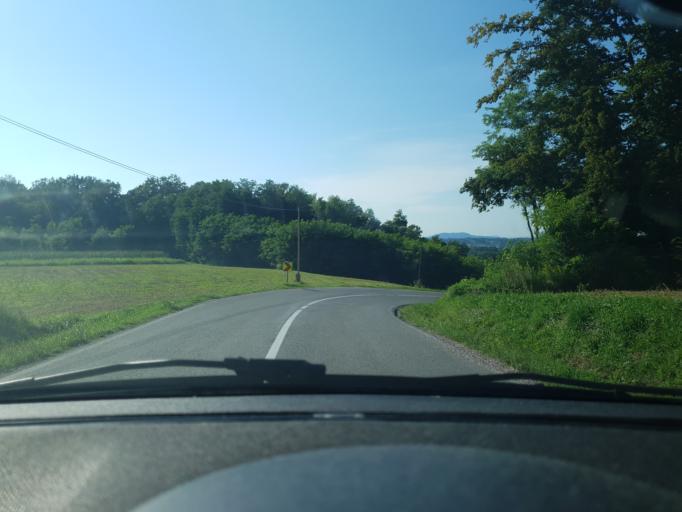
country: HR
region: Zagrebacka
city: Jakovlje
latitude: 45.9160
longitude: 15.8427
